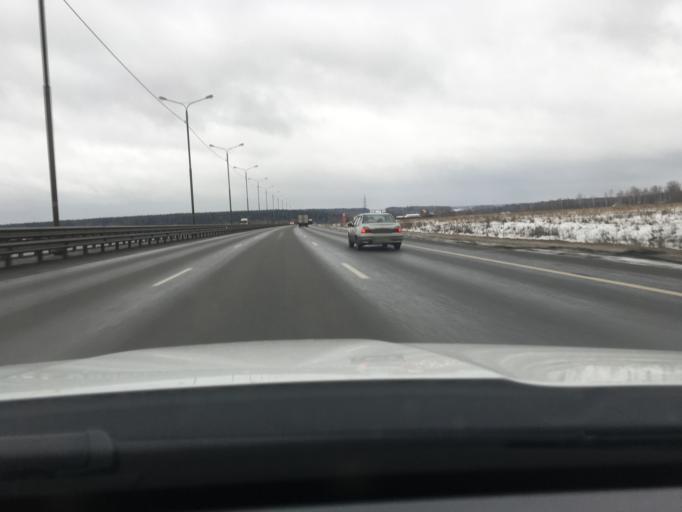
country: RU
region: Moskovskaya
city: Novyy Byt
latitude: 55.0907
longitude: 37.5836
